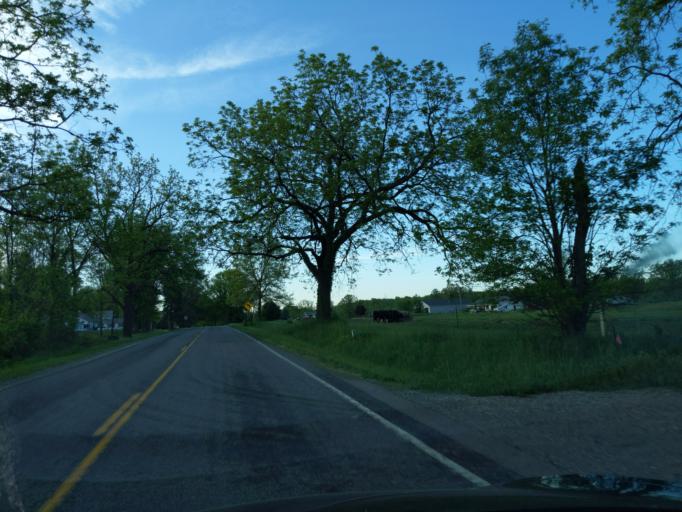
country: US
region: Michigan
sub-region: Ingham County
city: Leslie
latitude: 42.4607
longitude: -84.3142
